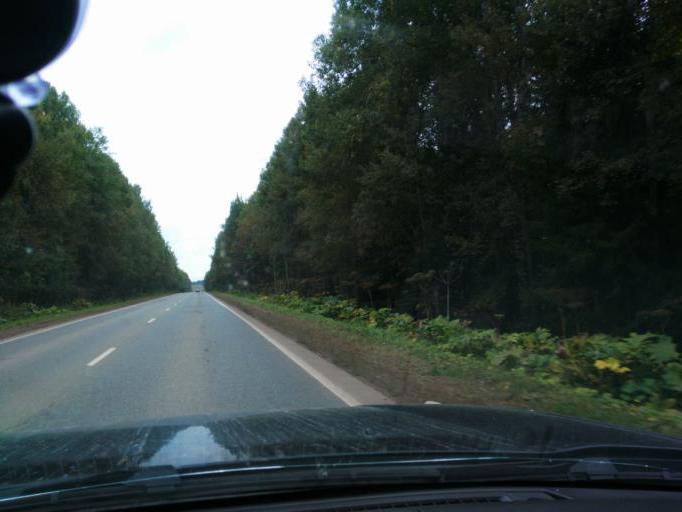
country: RU
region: Perm
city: Chernushka
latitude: 56.6455
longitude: 56.1614
